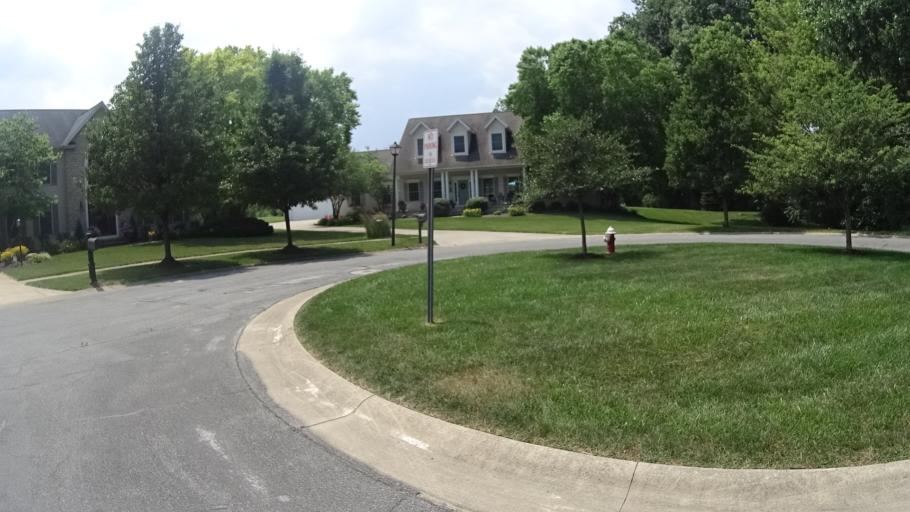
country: US
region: Ohio
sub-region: Erie County
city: Huron
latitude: 41.3859
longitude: -82.5343
